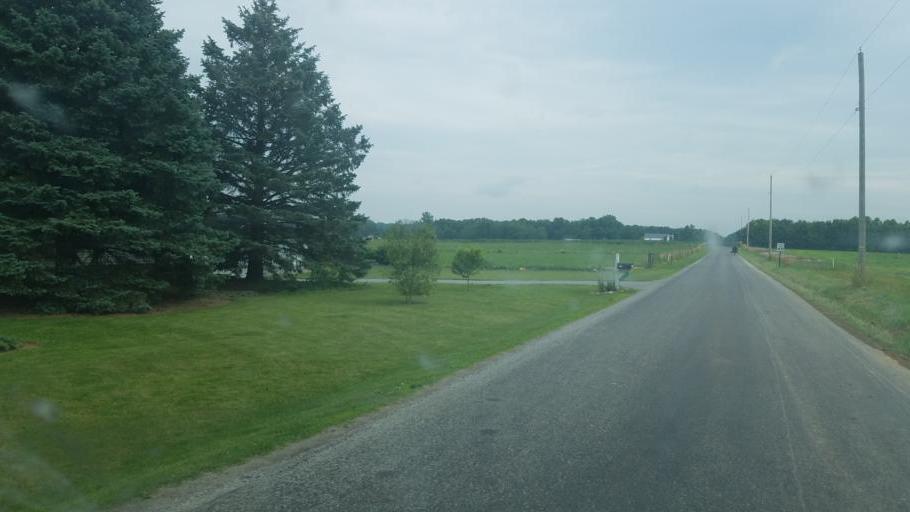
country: US
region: Ohio
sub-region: Wayne County
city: Orrville
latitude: 40.7818
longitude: -81.7752
